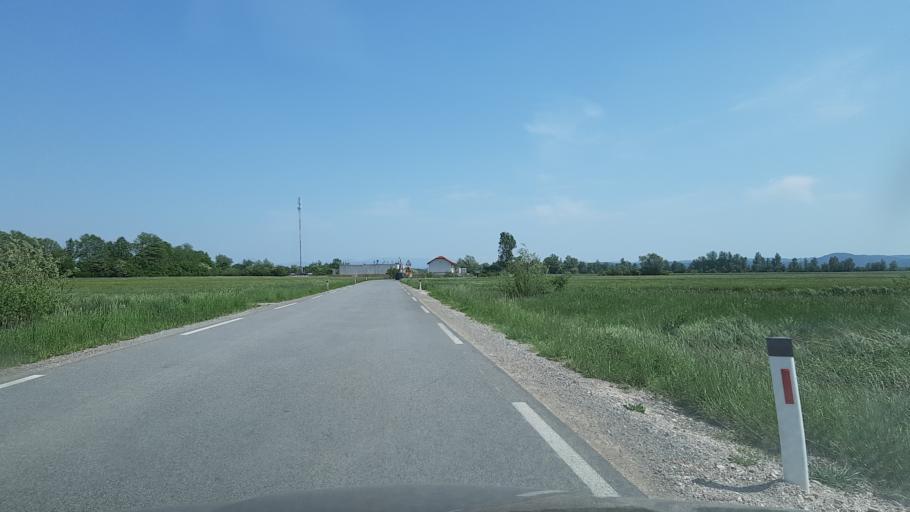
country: SI
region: Brezovica
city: Vnanje Gorice
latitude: 45.9793
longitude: 14.4272
